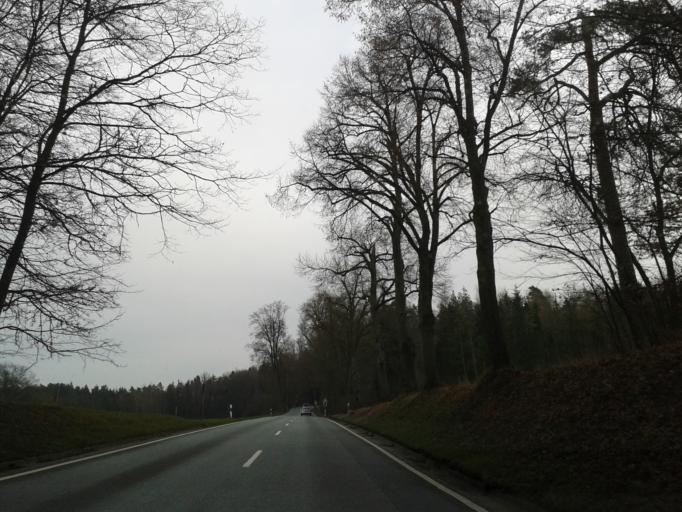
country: DE
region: Bavaria
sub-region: Upper Franconia
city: Weitramsdorf
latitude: 50.2329
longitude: 10.8767
